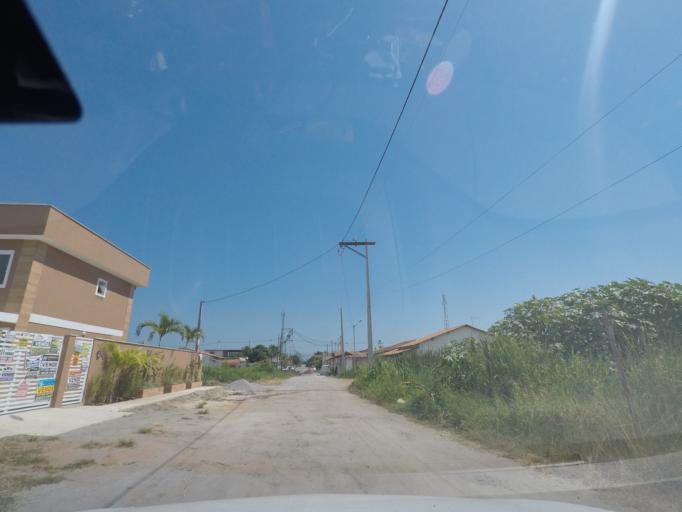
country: BR
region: Rio de Janeiro
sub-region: Marica
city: Marica
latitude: -22.9585
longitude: -42.9631
